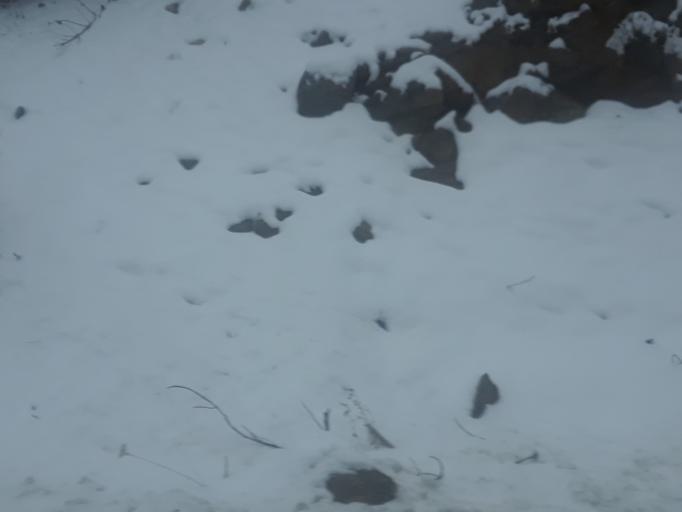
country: US
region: Colorado
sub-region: Boulder County
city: Coal Creek
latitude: 39.9235
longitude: -105.4197
